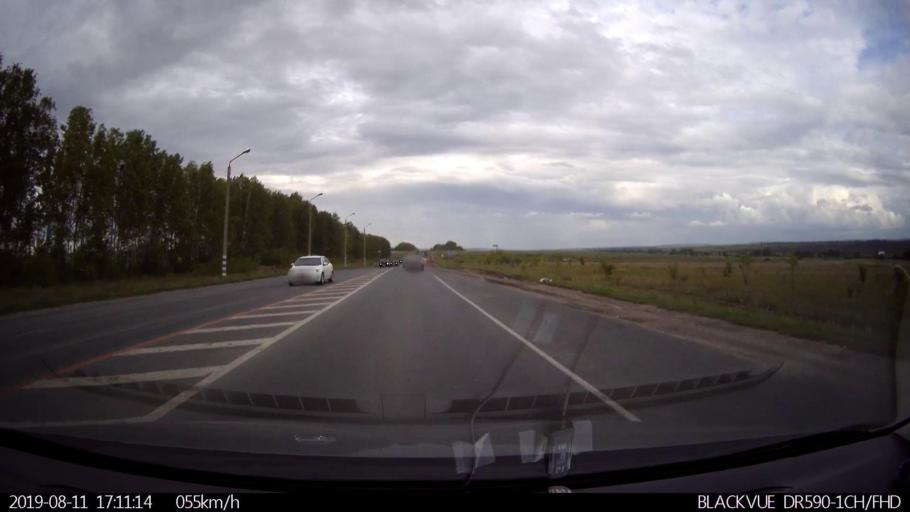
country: RU
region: Ulyanovsk
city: Mayna
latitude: 54.2999
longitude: 47.8837
